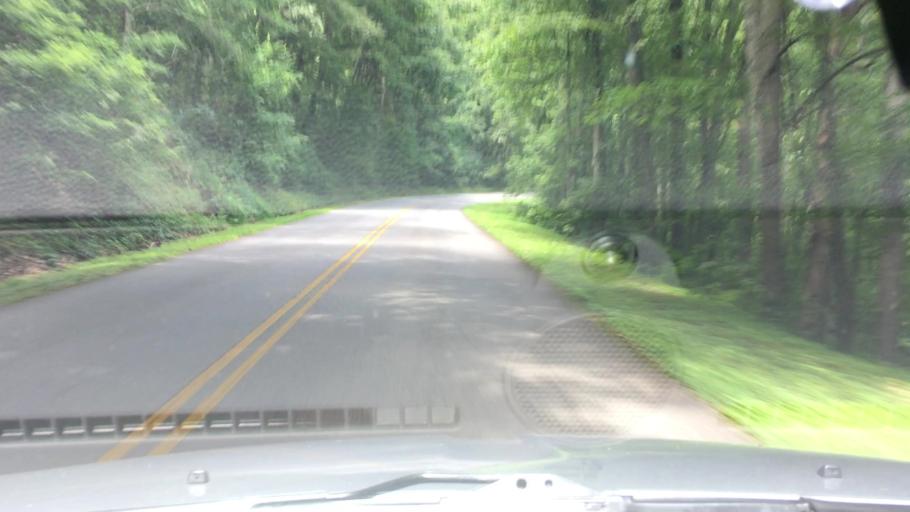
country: US
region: North Carolina
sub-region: Buncombe County
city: Asheville
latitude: 35.6314
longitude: -82.4961
